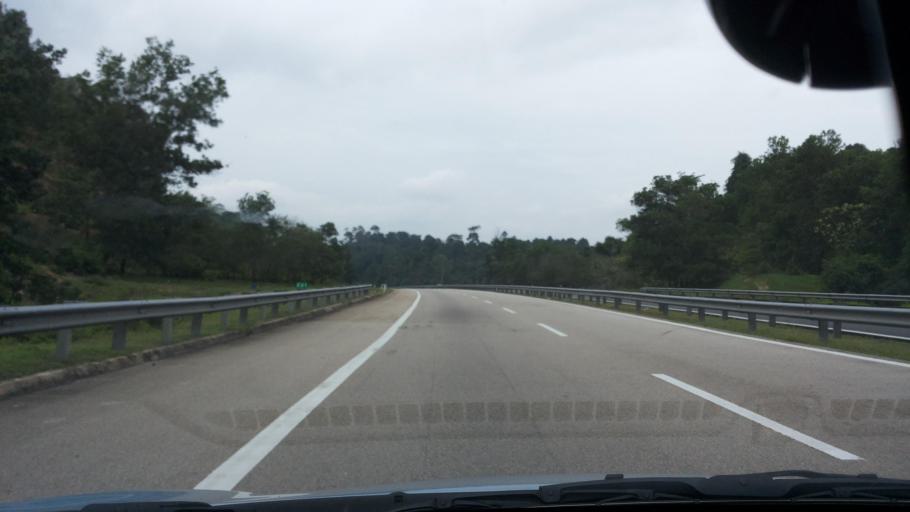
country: MY
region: Pahang
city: Kuantan
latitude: 3.7646
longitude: 103.1425
